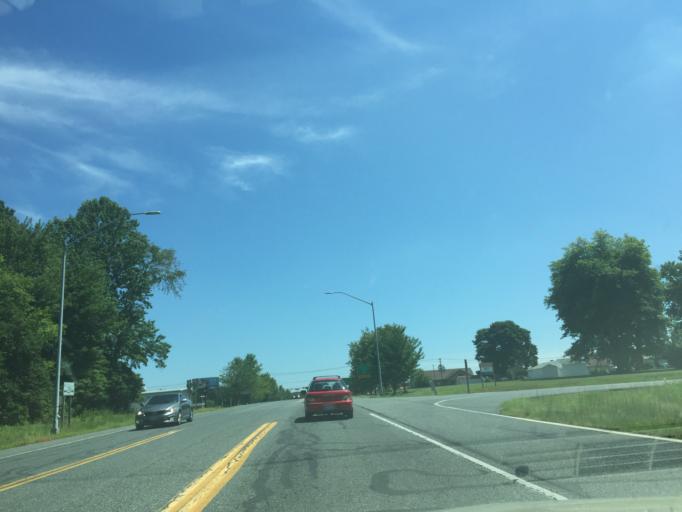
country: US
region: Maryland
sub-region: Harford County
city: Bel Air North
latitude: 39.5707
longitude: -76.3576
